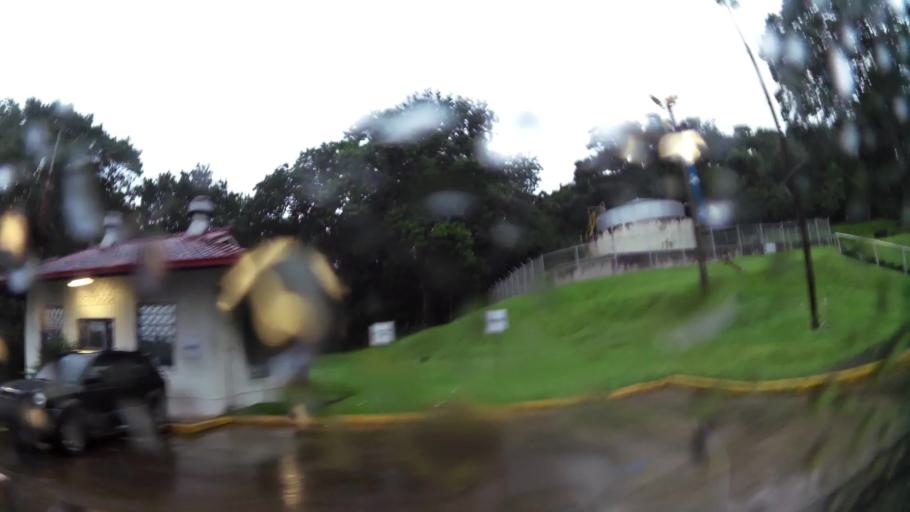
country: PA
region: Panama
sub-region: Distrito de Panama
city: Paraiso
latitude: 9.0018
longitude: -79.5911
